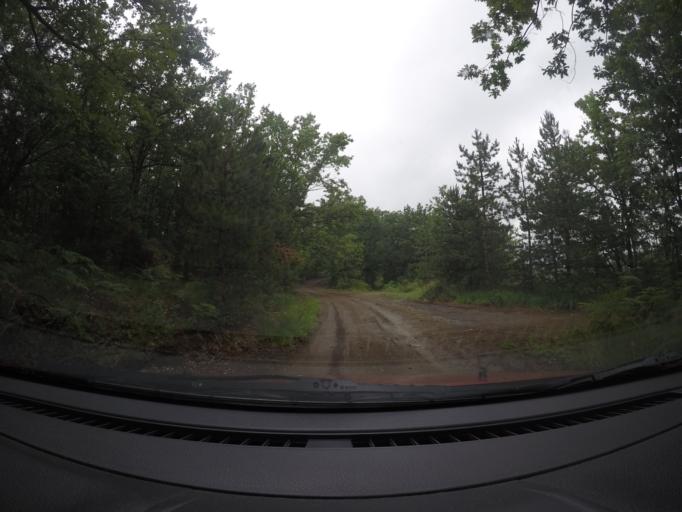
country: RS
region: Central Serbia
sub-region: Belgrade
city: Sopot
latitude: 44.5449
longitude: 20.5092
